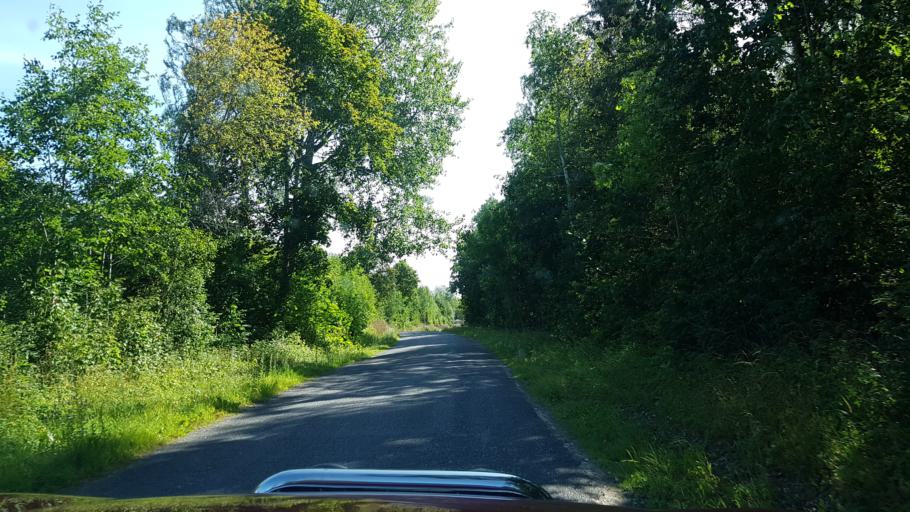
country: EE
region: Jaervamaa
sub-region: Jaerva-Jaani vald
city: Jarva-Jaani
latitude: 59.1177
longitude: 25.6743
